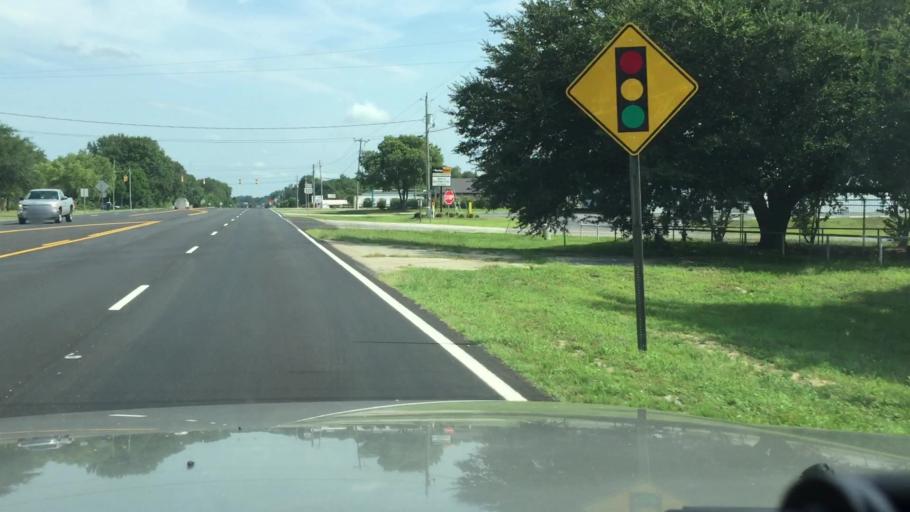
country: US
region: South Carolina
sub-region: Sumter County
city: South Sumter
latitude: 33.8871
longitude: -80.3504
